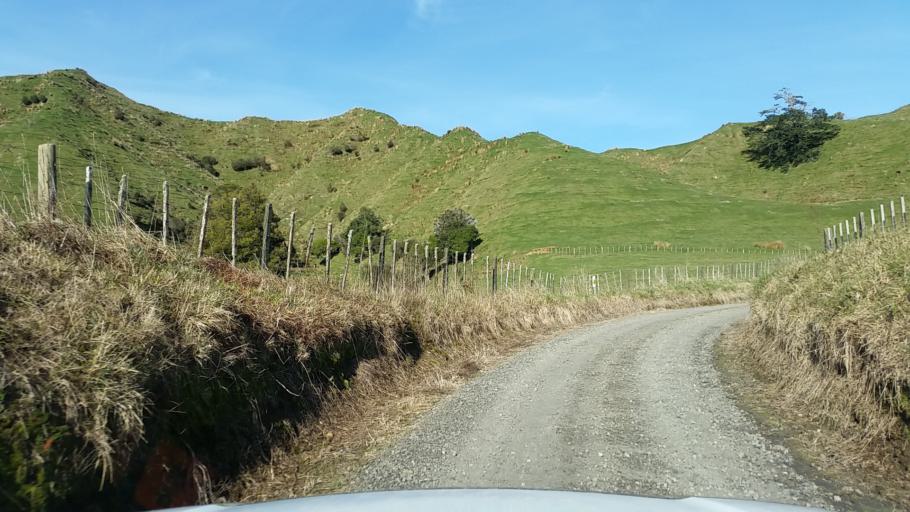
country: NZ
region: Taranaki
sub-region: South Taranaki District
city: Eltham
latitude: -39.3109
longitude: 174.5496
